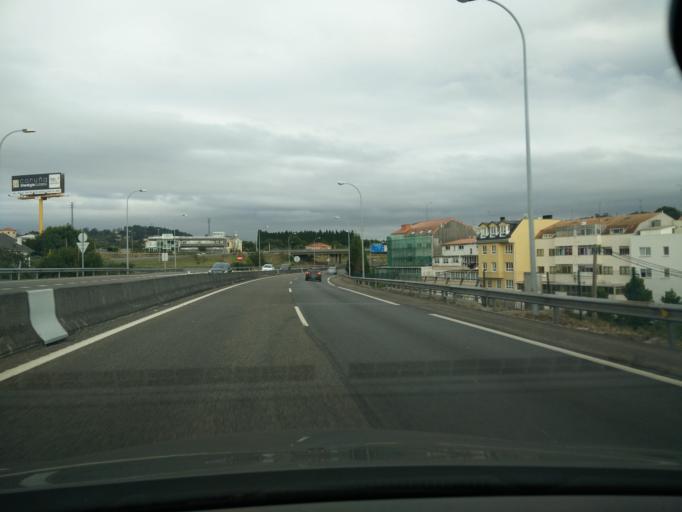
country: ES
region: Galicia
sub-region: Provincia da Coruna
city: Cambre
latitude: 43.3119
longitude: -8.3554
